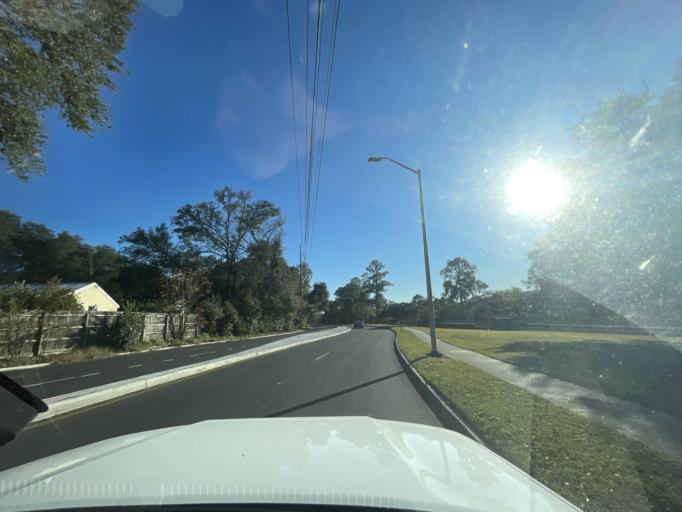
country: US
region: Louisiana
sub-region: East Baton Rouge Parish
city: Baton Rouge
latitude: 30.4322
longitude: -91.1527
